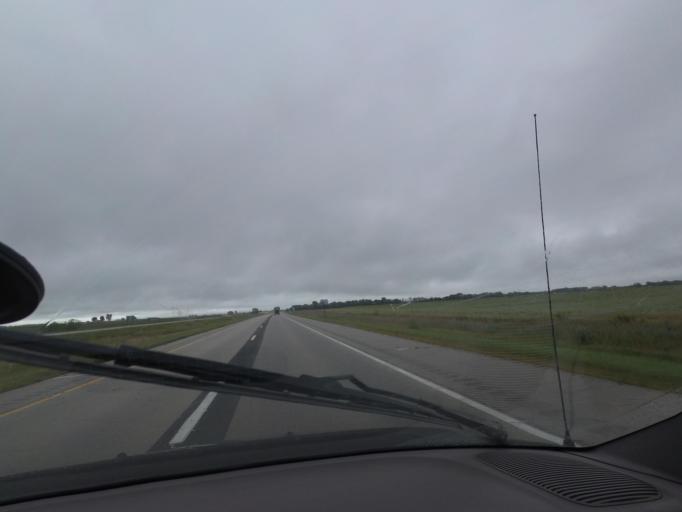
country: US
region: Illinois
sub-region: Sangamon County
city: Riverton
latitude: 39.8385
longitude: -89.3965
